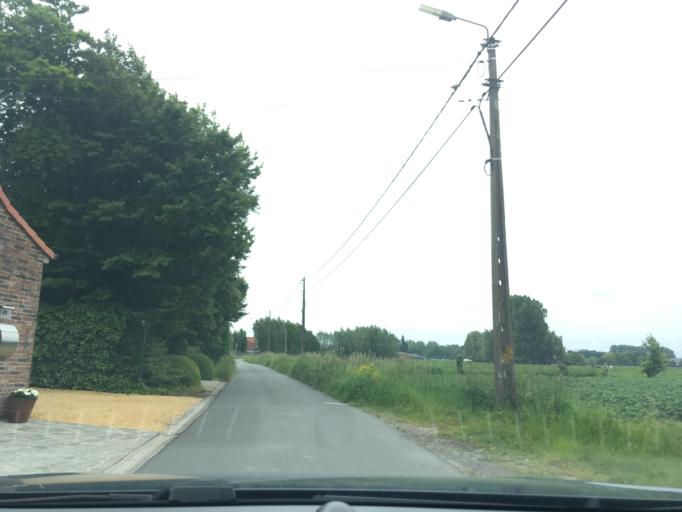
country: BE
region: Flanders
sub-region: Provincie West-Vlaanderen
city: Ledegem
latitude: 50.8616
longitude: 3.0918
